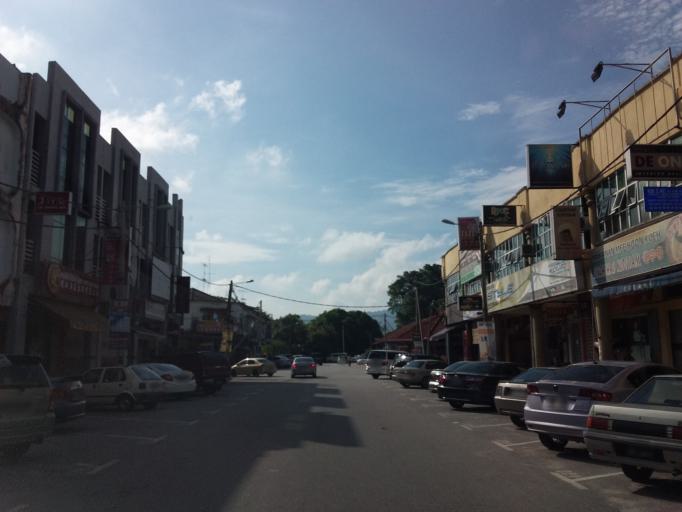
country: MY
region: Johor
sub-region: Daerah Batu Pahat
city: Batu Pahat
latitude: 1.8522
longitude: 102.9301
